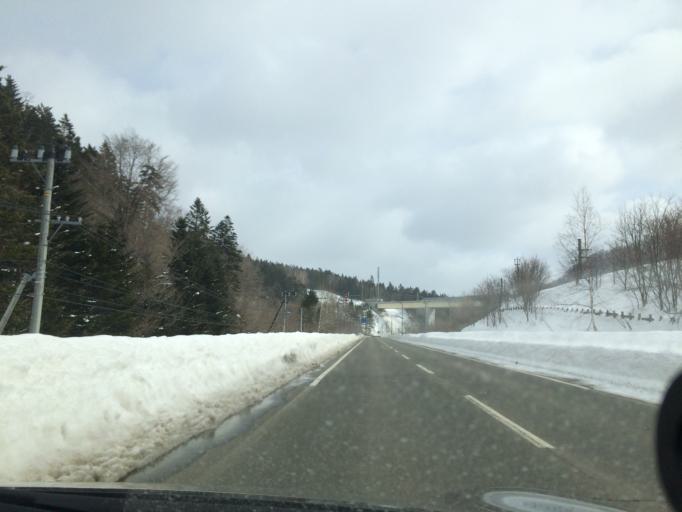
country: JP
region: Hokkaido
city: Shimo-furano
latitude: 43.0536
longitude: 142.4921
